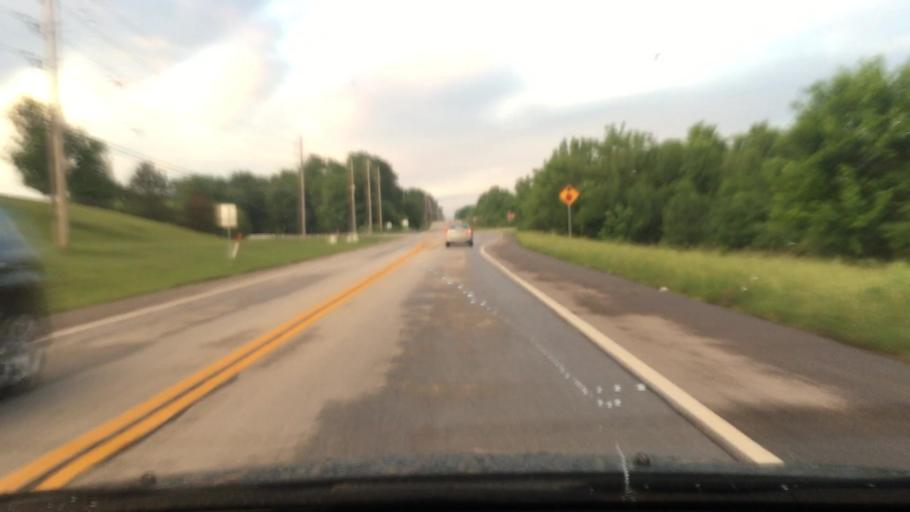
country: US
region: Missouri
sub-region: Jackson County
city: Lees Summit
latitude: 38.8700
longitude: -94.4163
